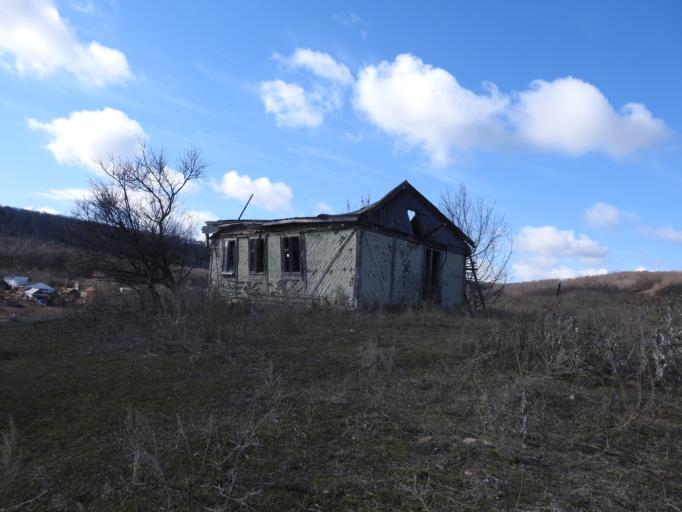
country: RU
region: Saratov
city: Krasnyy Oktyabr'
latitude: 51.3843
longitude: 45.7415
